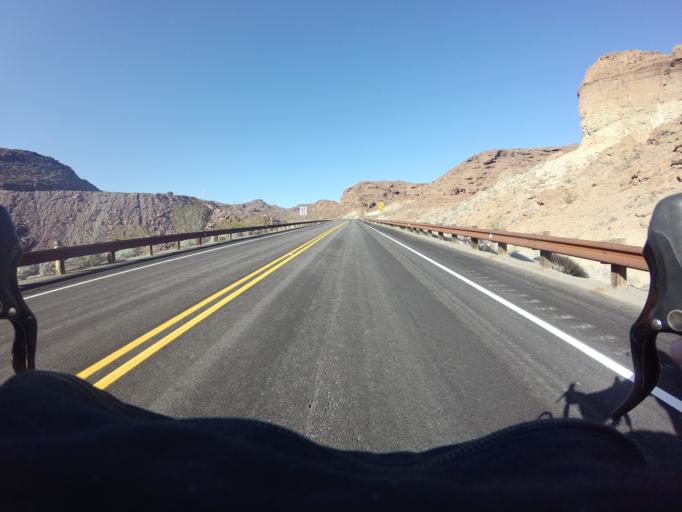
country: US
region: Nevada
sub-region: Clark County
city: Boulder City
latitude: 36.0114
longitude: -114.7297
